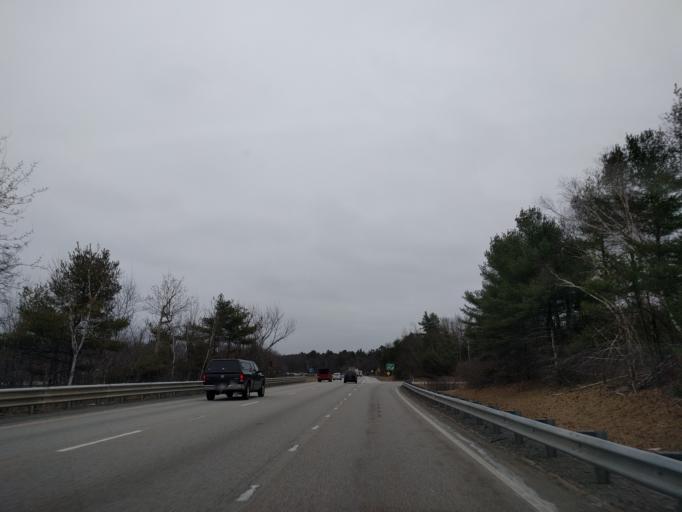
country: US
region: Massachusetts
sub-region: Worcester County
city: Westminster
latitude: 42.5431
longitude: -71.8968
